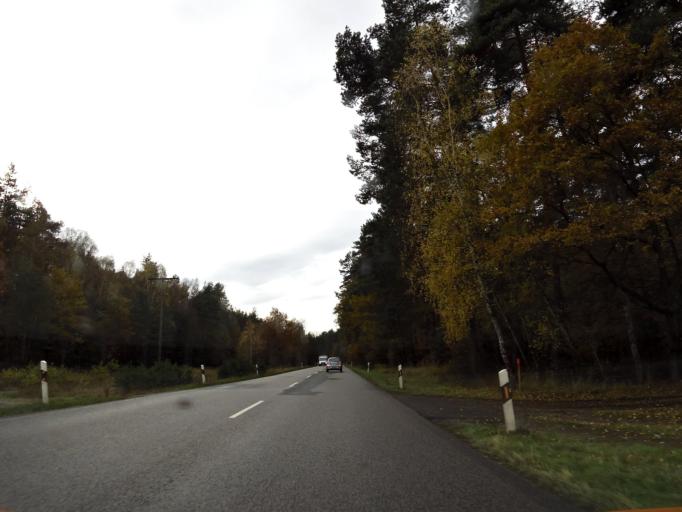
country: DE
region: Saxony-Anhalt
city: Haldensleben I
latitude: 52.3503
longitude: 11.4612
